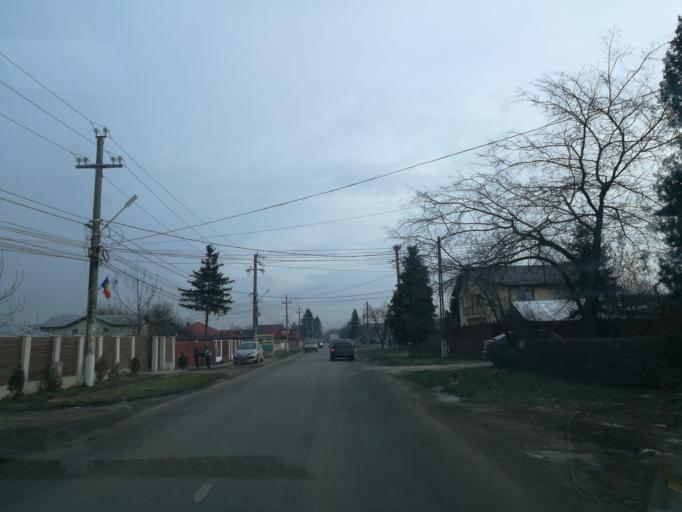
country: RO
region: Ilfov
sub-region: Comuna Moara Vlasiei
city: Moara Vlasiei
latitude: 44.6406
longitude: 26.2094
